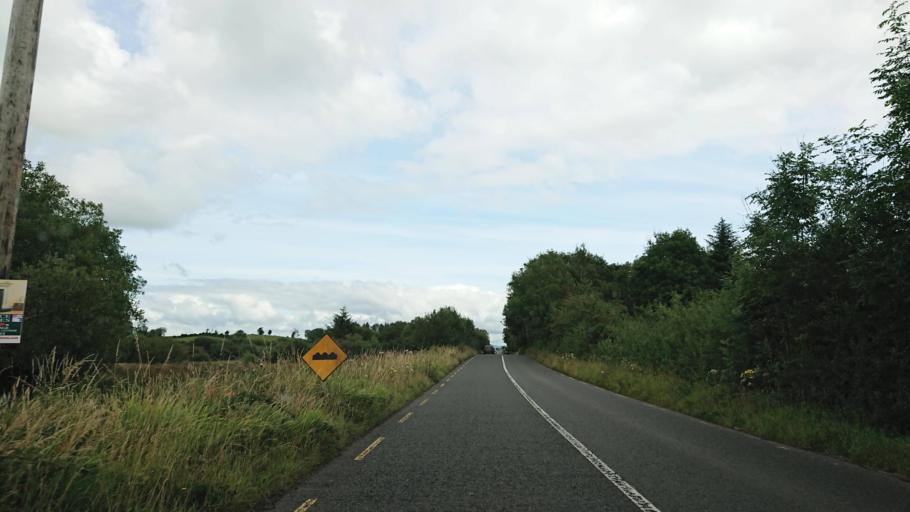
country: IE
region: Connaught
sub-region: County Leitrim
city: Carrick-on-Shannon
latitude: 54.0601
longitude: -8.0973
